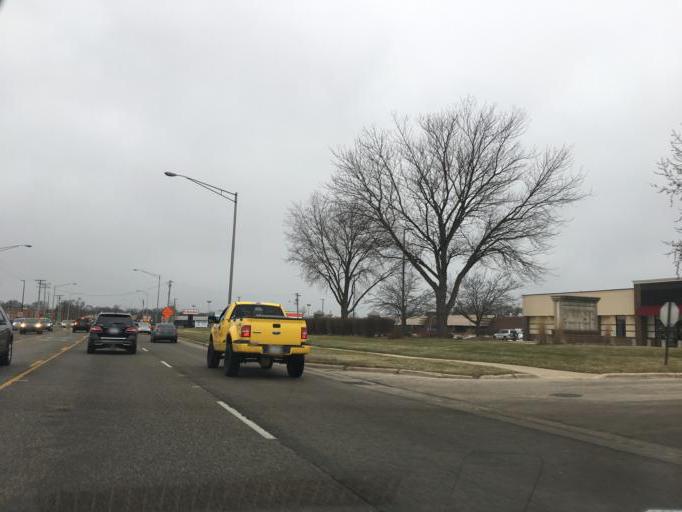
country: US
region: Illinois
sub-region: McHenry County
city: Crystal Lake
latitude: 42.2262
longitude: -88.3214
